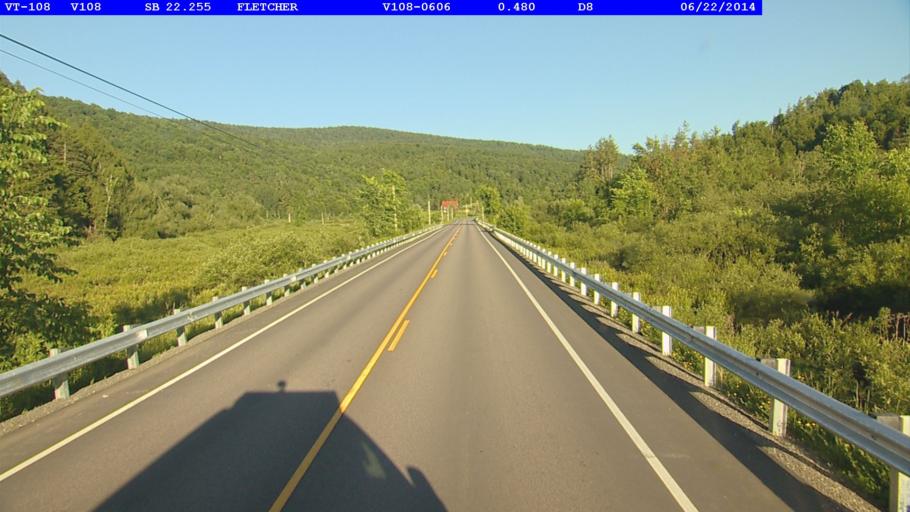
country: US
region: Vermont
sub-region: Lamoille County
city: Johnson
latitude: 44.7095
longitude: -72.8362
